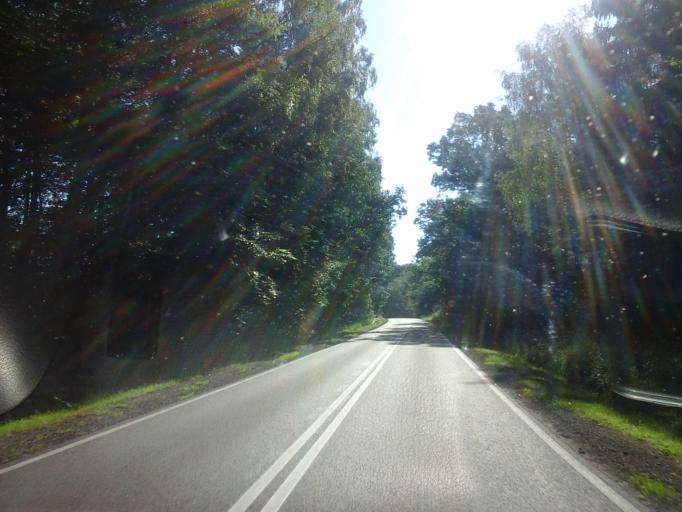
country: PL
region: West Pomeranian Voivodeship
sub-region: Powiat drawski
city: Drawsko Pomorskie
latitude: 53.4911
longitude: 15.7163
